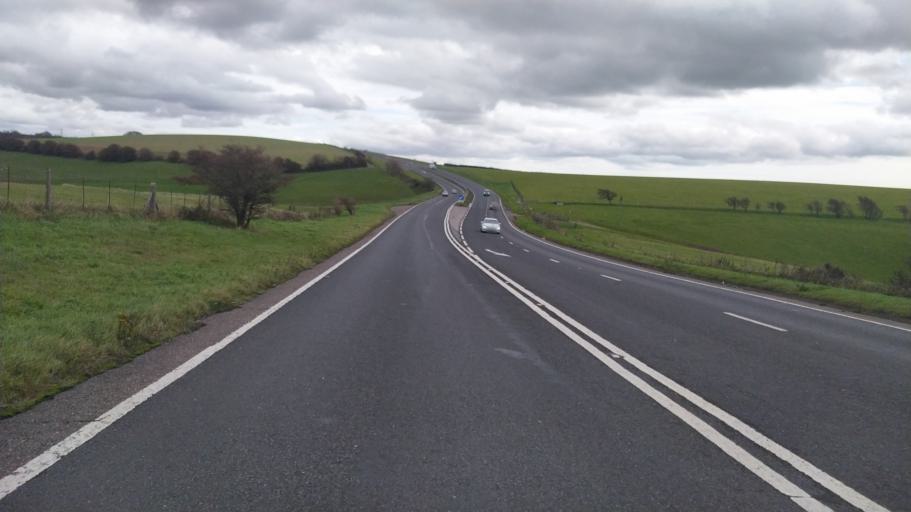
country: GB
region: England
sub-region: Dorset
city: Bridport
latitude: 50.7249
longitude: -2.6491
